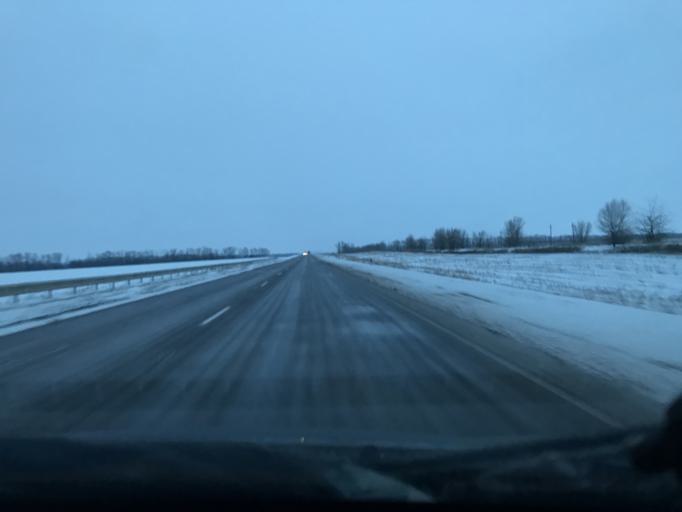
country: RU
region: Rostov
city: Letnik
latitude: 45.9821
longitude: 41.2389
